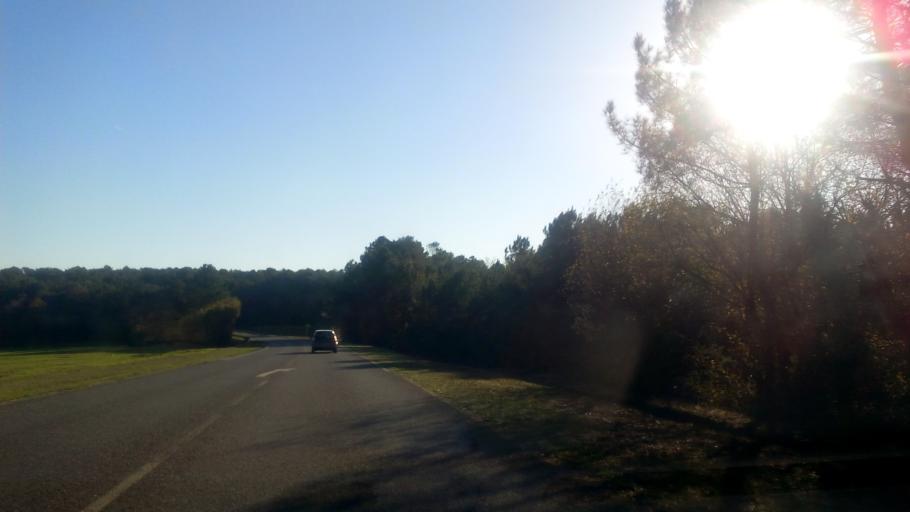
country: FR
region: Brittany
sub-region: Departement du Morbihan
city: Saint-Vincent-sur-Oust
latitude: 47.6859
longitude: -2.1389
